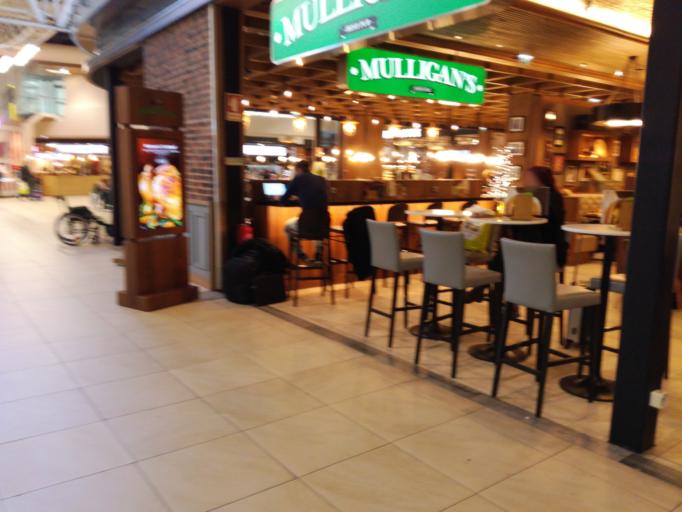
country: PT
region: Faro
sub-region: Faro
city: Faro
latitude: 37.0200
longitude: -7.9683
